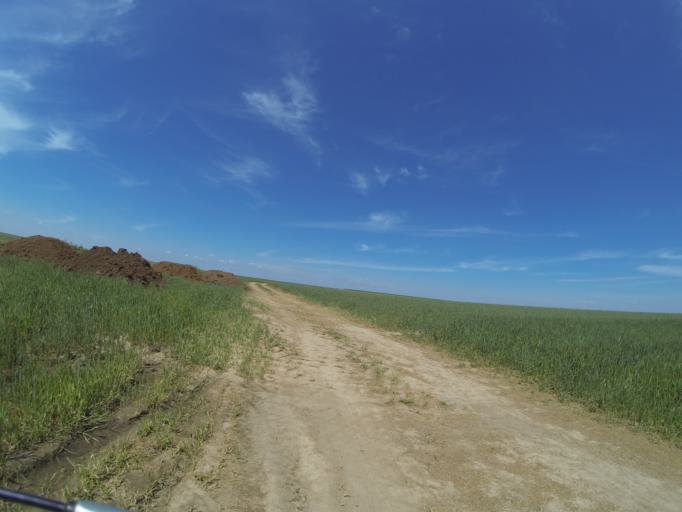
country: RO
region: Dolj
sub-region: Comuna Teslui
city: Teslui
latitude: 44.1839
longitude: 24.1721
